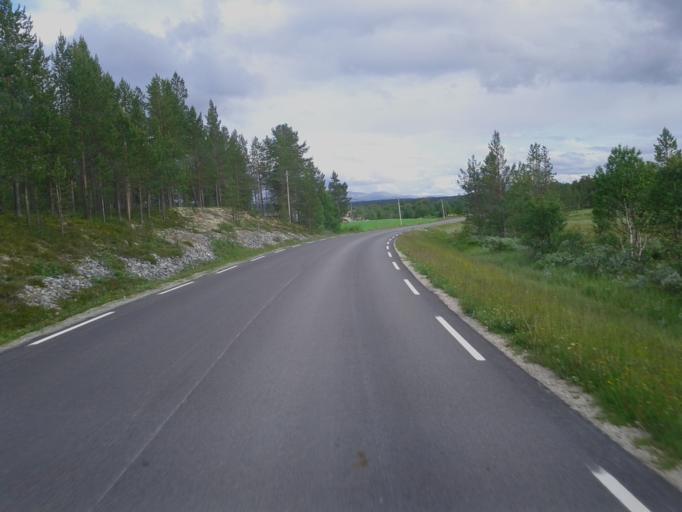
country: NO
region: Sor-Trondelag
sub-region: Roros
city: Roros
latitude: 62.3030
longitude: 11.7181
